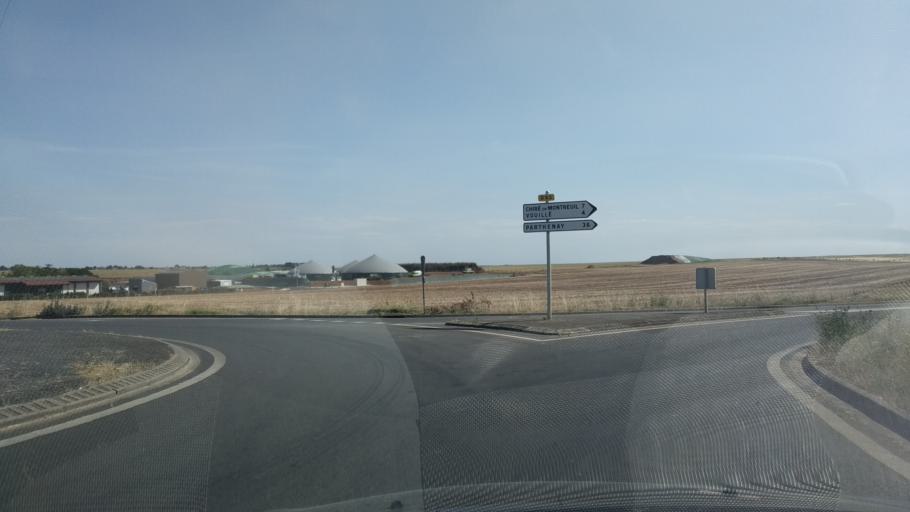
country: FR
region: Poitou-Charentes
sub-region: Departement de la Vienne
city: Cisse
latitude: 46.6646
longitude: 0.2039
